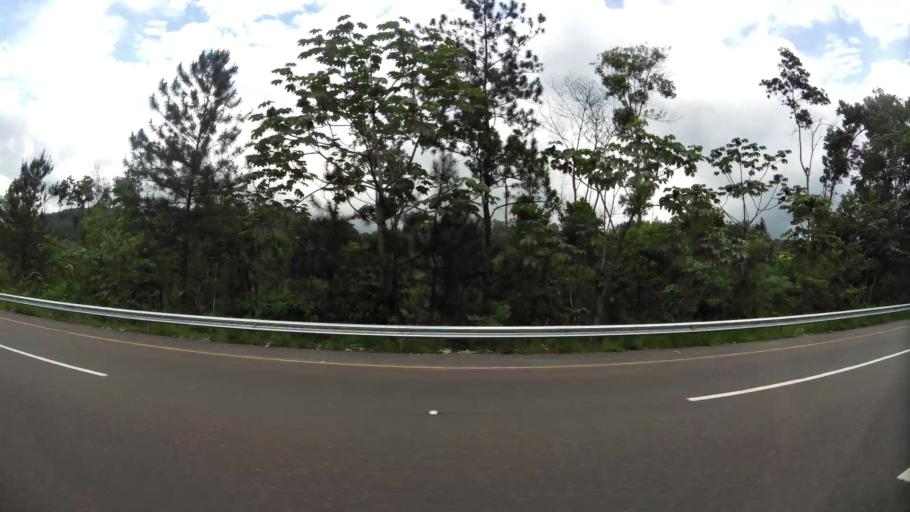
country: DO
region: Monsenor Nouel
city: Piedra Blanca
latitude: 18.7982
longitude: -70.2743
